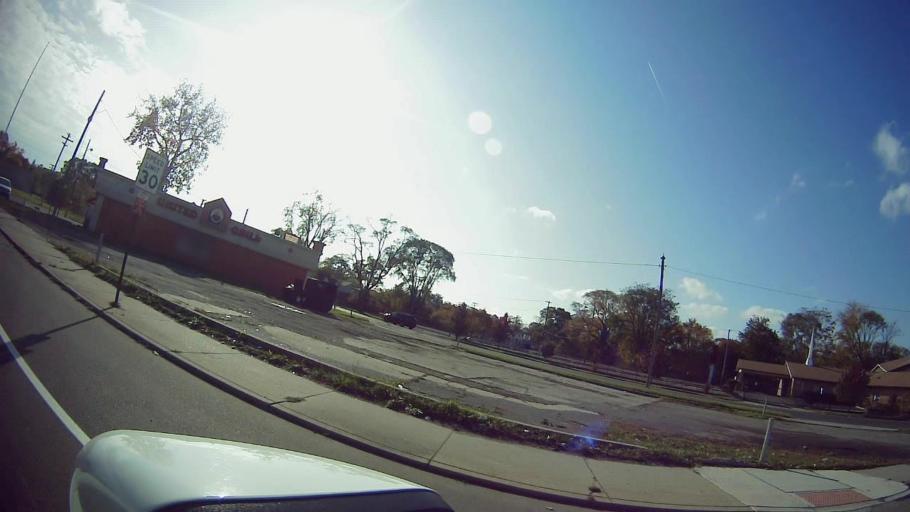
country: US
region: Michigan
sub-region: Wayne County
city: Highland Park
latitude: 42.4311
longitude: -83.0724
